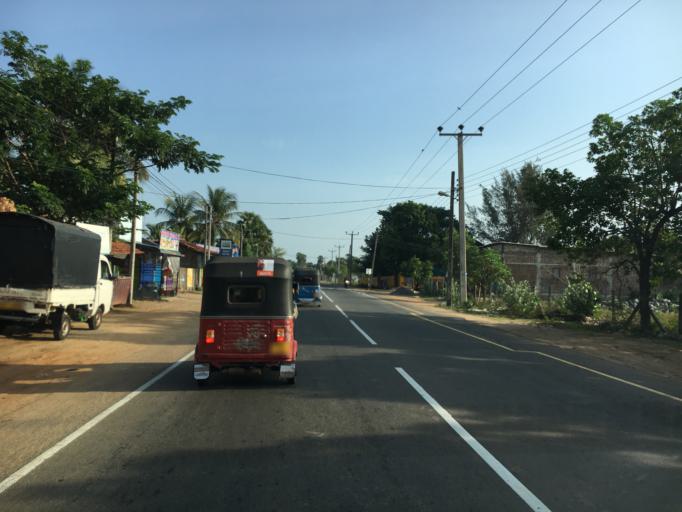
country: LK
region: Eastern Province
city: Eravur Town
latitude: 7.9254
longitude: 81.5136
